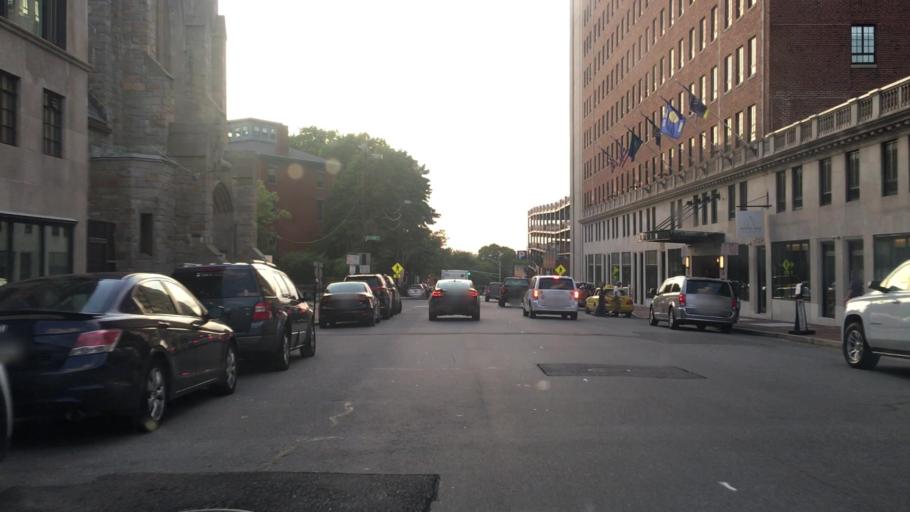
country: US
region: Maine
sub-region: Cumberland County
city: Portland
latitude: 43.6543
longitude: -70.2637
